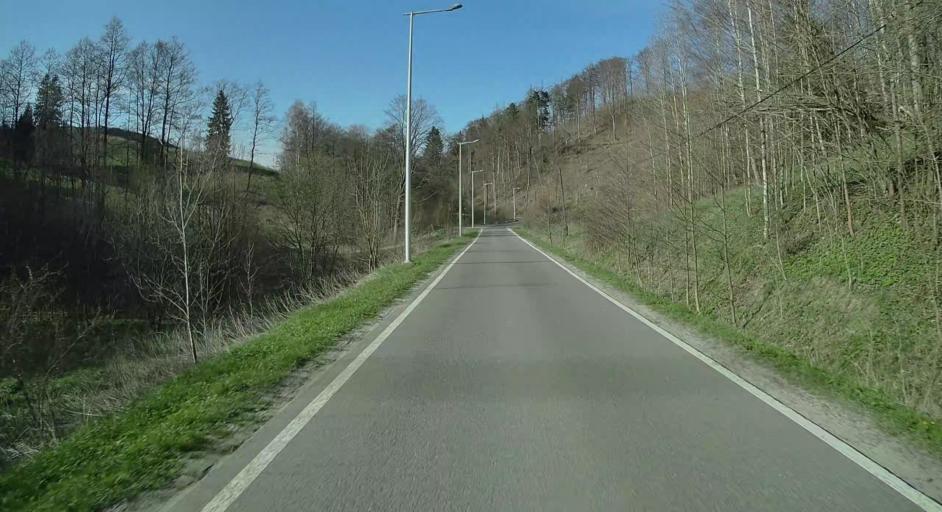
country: PL
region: Lower Silesian Voivodeship
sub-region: Powiat klodzki
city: Lewin Klodzki
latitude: 50.3907
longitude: 16.3006
